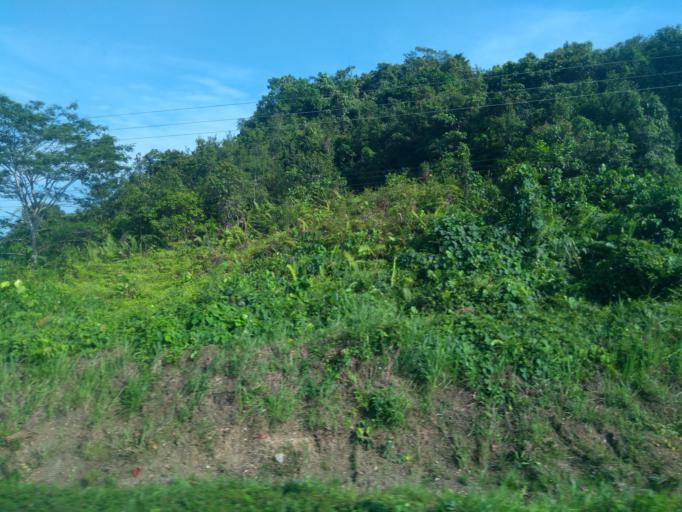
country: MY
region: Sarawak
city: Kuching
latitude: 1.6346
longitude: 110.4512
